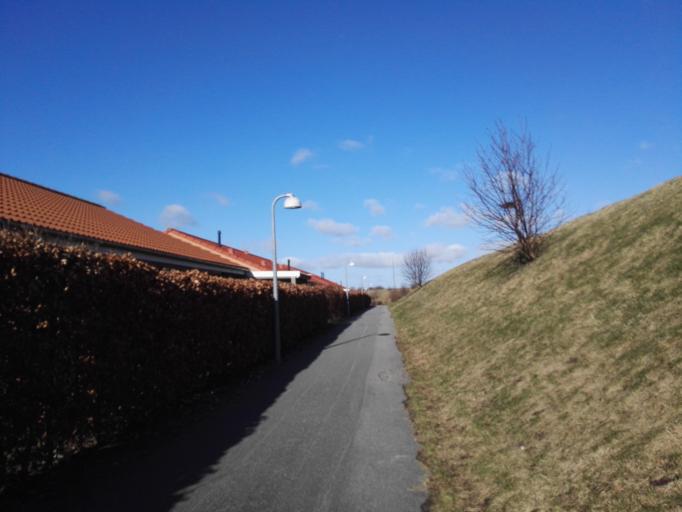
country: DK
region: Capital Region
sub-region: Egedal Kommune
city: Stenlose
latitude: 55.7747
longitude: 12.1870
